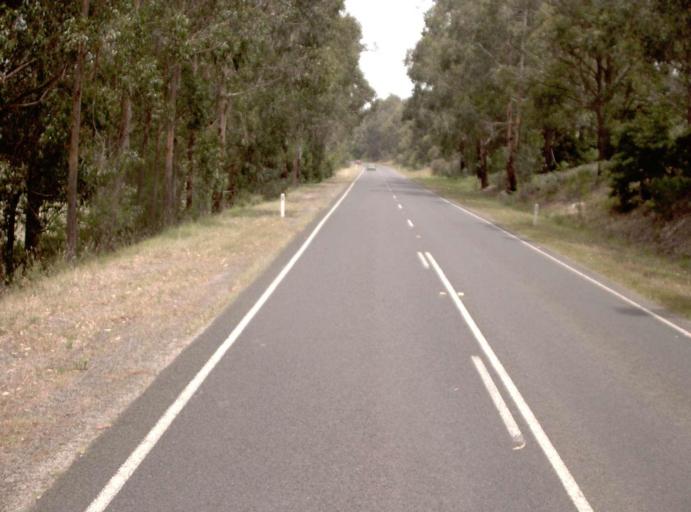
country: AU
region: Victoria
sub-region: Latrobe
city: Traralgon
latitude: -38.4619
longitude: 146.7229
